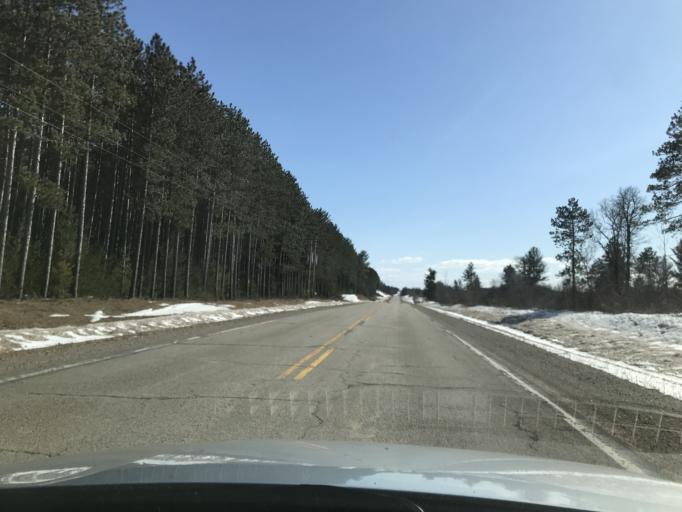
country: US
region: Wisconsin
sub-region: Marinette County
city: Niagara
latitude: 45.3841
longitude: -88.0997
